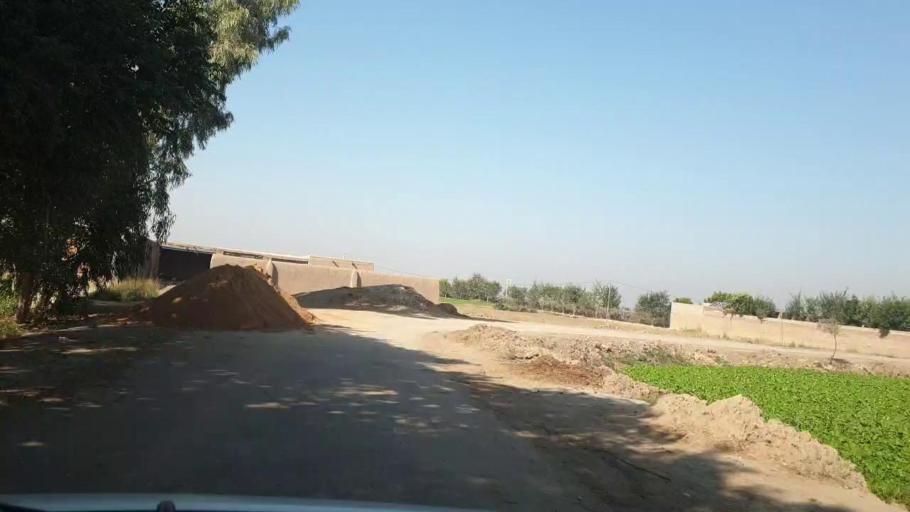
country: PK
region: Sindh
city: Bhan
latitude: 26.6069
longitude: 67.7343
